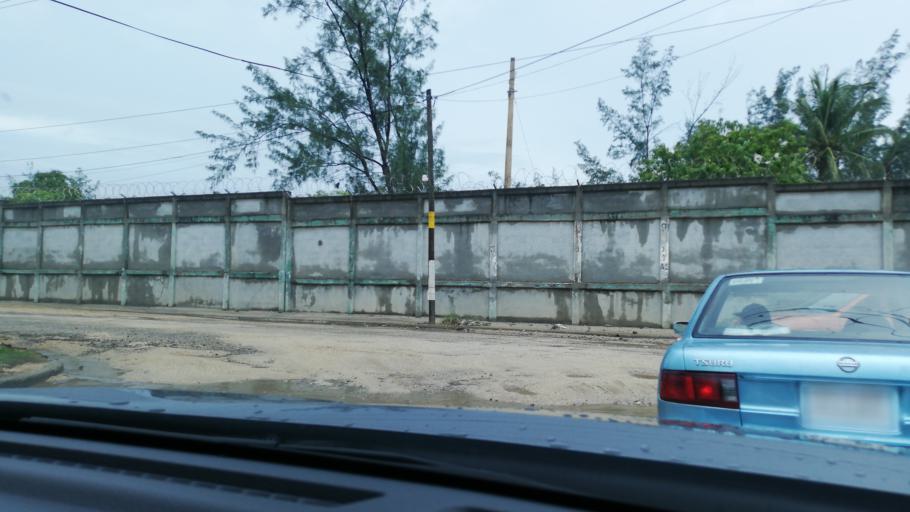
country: MX
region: Oaxaca
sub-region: Salina Cruz
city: Salina Cruz
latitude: 16.1965
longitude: -95.1925
